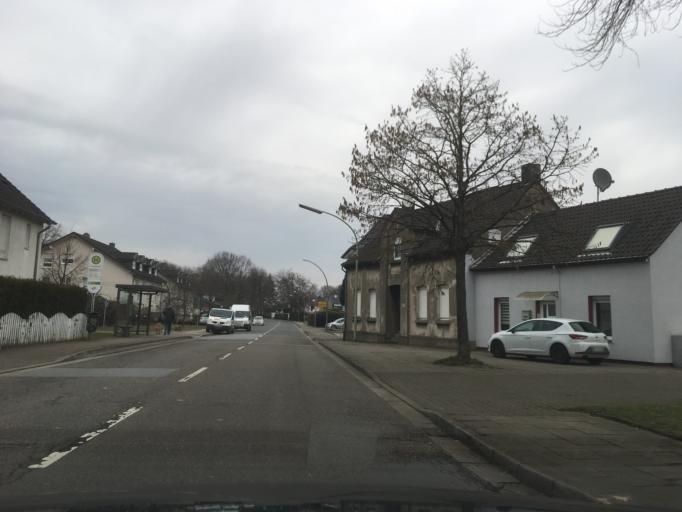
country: DE
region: North Rhine-Westphalia
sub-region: Regierungsbezirk Munster
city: Gladbeck
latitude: 51.5446
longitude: 7.0283
